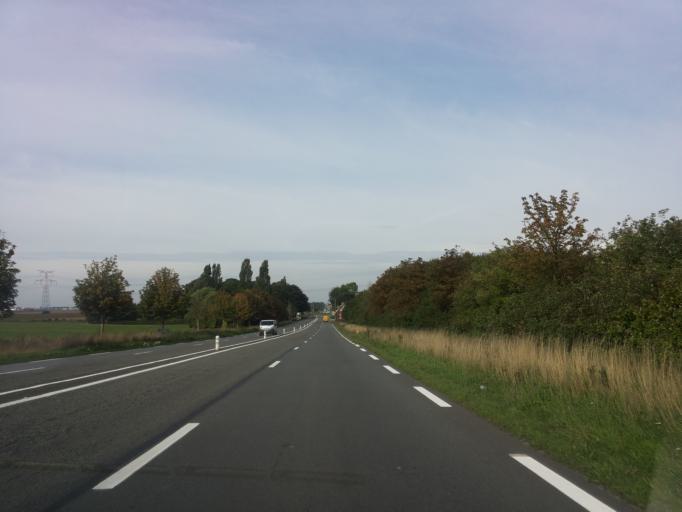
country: FR
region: Nord-Pas-de-Calais
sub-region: Departement du Pas-de-Calais
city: Feuchy
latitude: 50.2703
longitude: 2.8528
